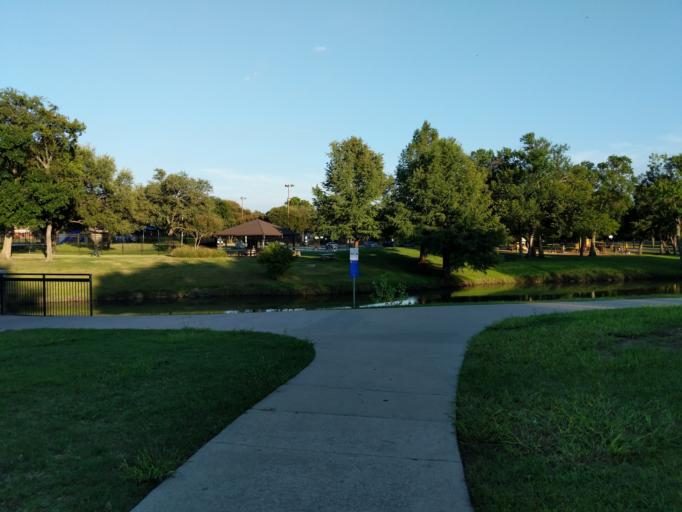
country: US
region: Texas
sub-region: Dallas County
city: Richardson
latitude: 32.9496
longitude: -96.7661
